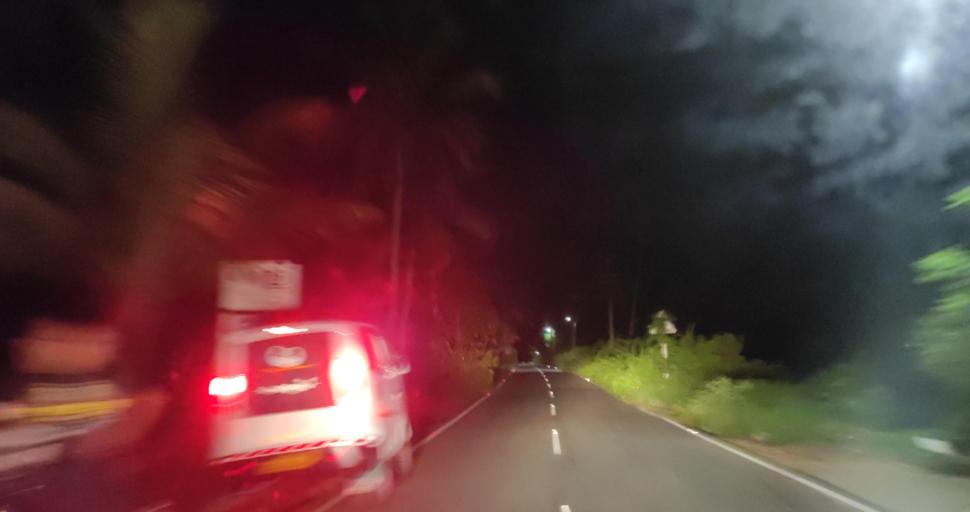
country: IN
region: Kerala
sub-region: Alappuzha
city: Vayalar
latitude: 9.7463
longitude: 76.2910
